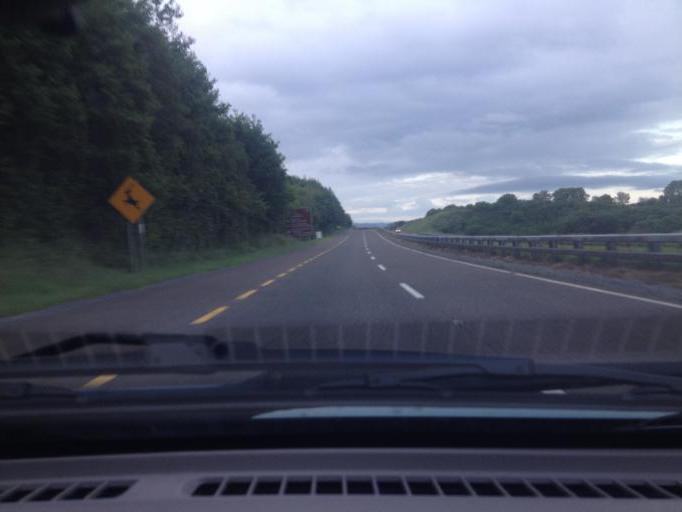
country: IE
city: Ballisodare
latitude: 54.2289
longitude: -8.4970
